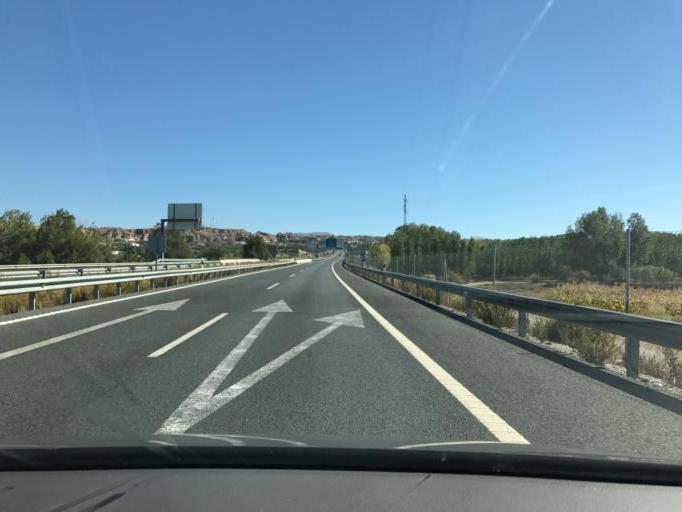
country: ES
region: Andalusia
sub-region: Provincia de Granada
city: Guadix
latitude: 37.3206
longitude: -3.1578
